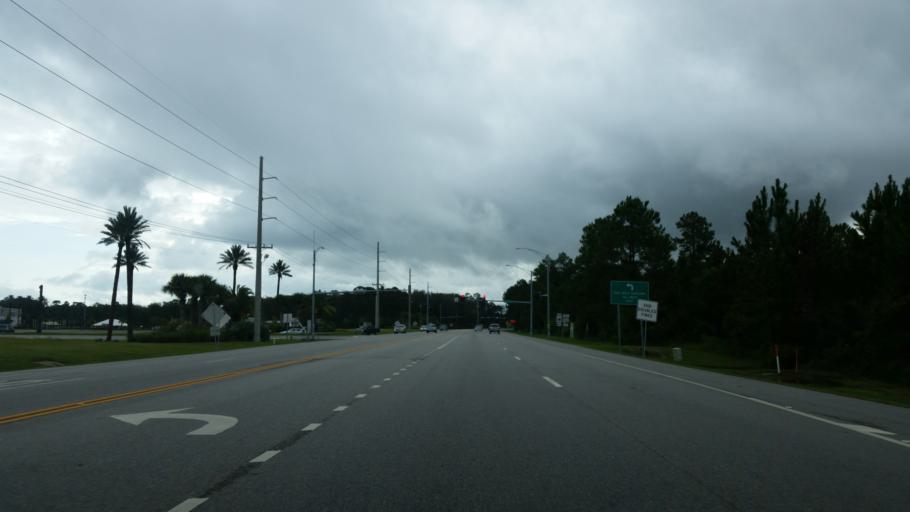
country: US
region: Alabama
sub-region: Baldwin County
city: Orange Beach
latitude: 30.2896
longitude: -87.6308
